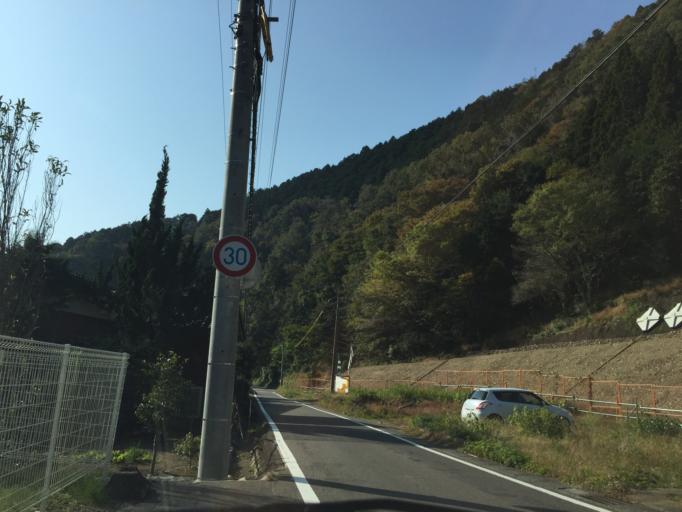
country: JP
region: Gifu
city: Minokamo
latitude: 35.5477
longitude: 137.1192
